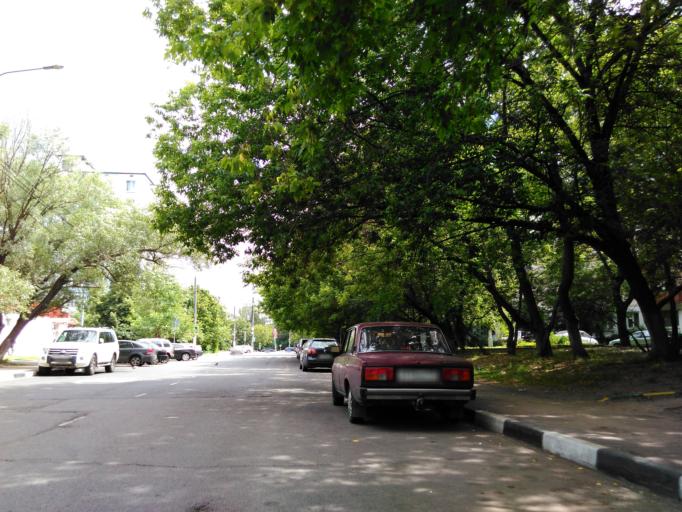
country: RU
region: Moscow
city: Zyuzino
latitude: 55.6608
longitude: 37.5722
